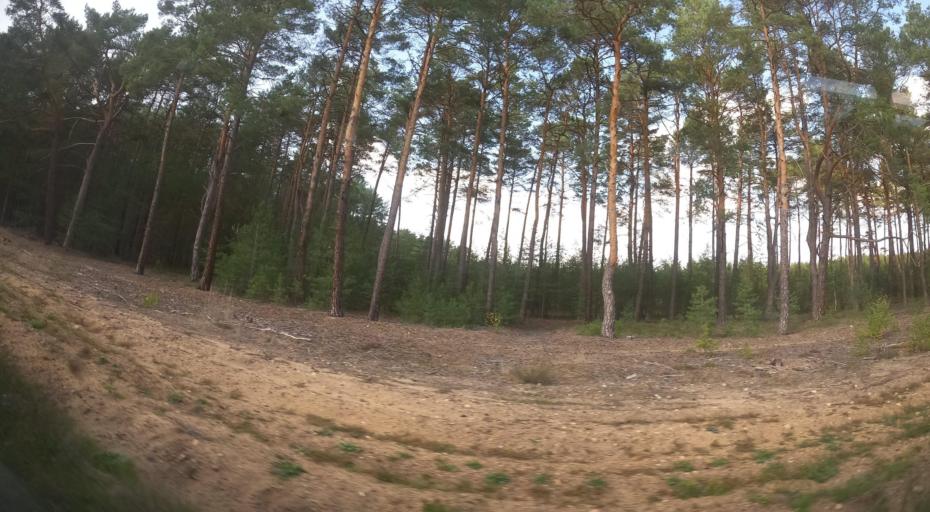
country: PL
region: Lubusz
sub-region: Powiat zielonogorski
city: Swidnica
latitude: 51.8616
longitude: 15.3070
